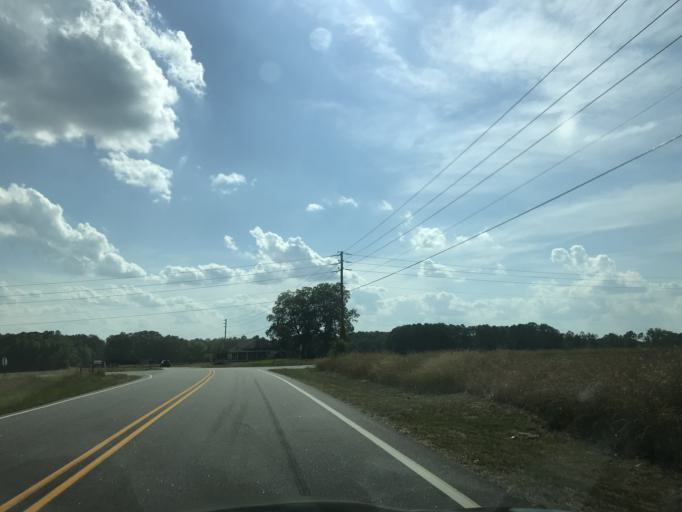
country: US
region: North Carolina
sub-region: Nash County
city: Spring Hope
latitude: 35.9599
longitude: -78.0705
